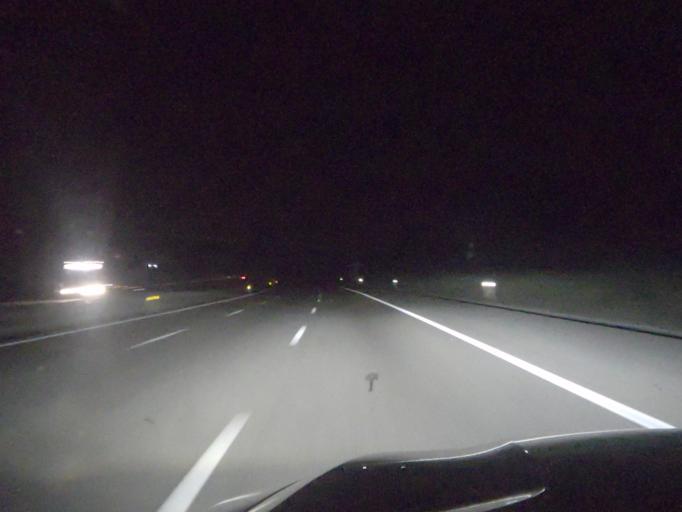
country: PT
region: Santarem
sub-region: Alcanena
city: Alcanena
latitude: 39.4336
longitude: -8.6275
